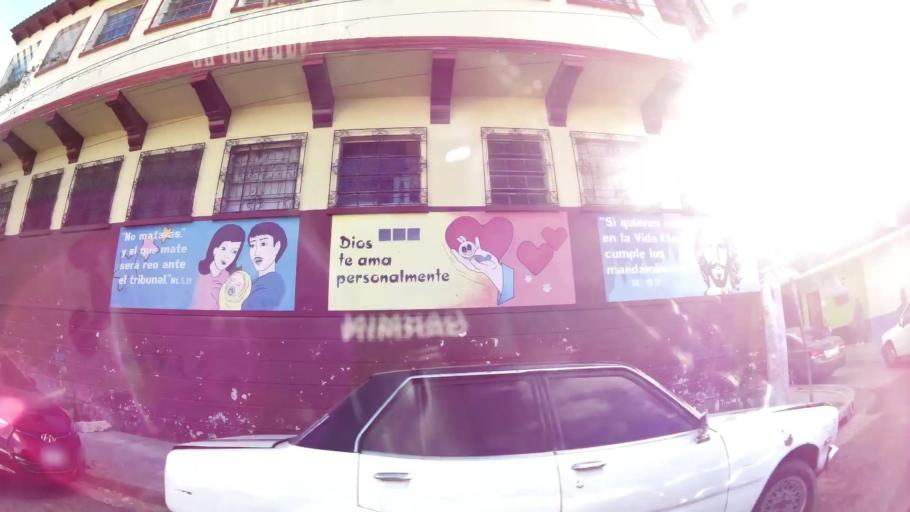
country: SV
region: Cuscatlan
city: Cojutepeque
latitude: 13.7225
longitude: -88.9362
